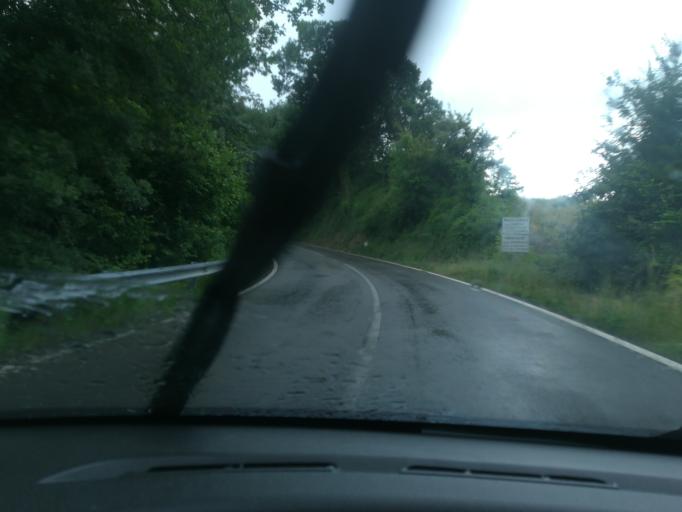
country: IT
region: The Marches
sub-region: Provincia di Macerata
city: Sarnano
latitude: 43.0134
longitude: 13.3262
